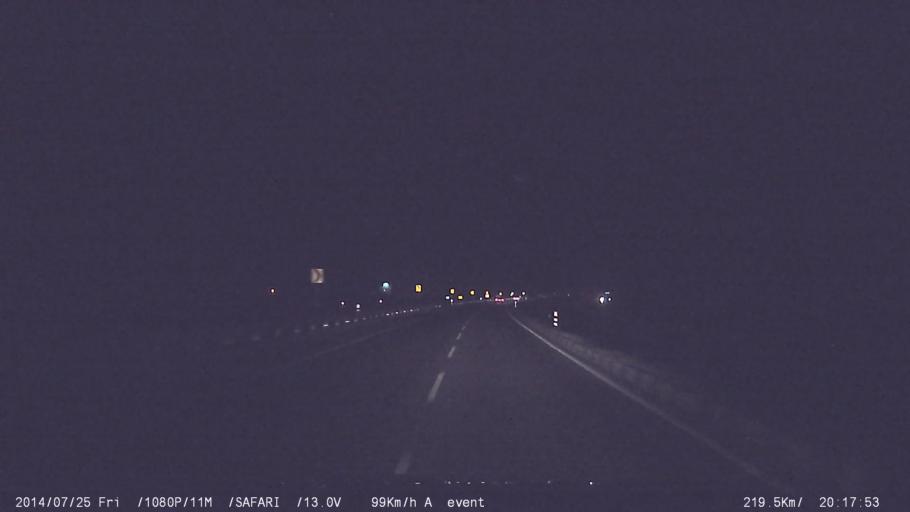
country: IN
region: Tamil Nadu
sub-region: Salem
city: Konganapuram
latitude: 11.5367
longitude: 77.9660
